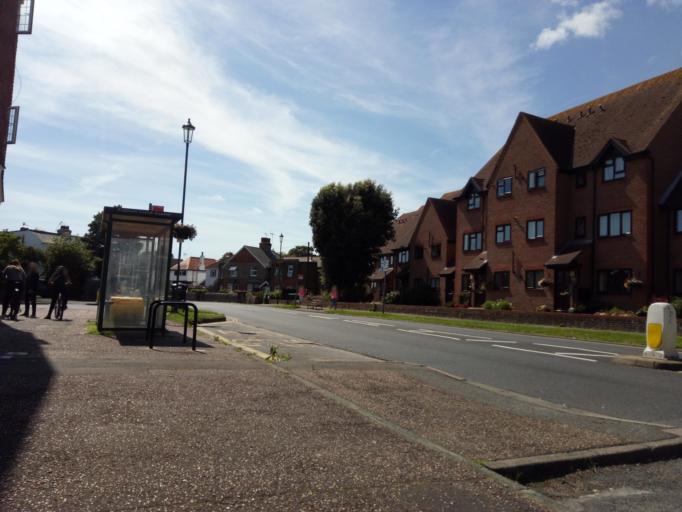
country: GB
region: England
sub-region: West Sussex
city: Bognor Regis
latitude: 50.7891
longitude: -0.6546
